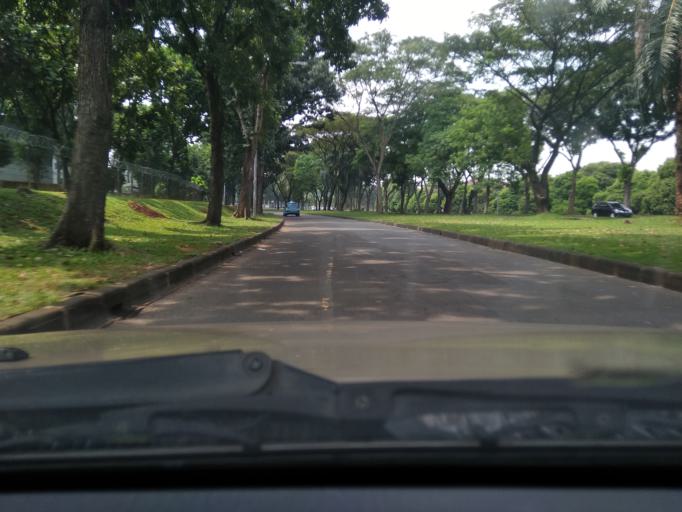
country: ID
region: West Java
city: Serpong
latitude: -6.2982
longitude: 106.6746
